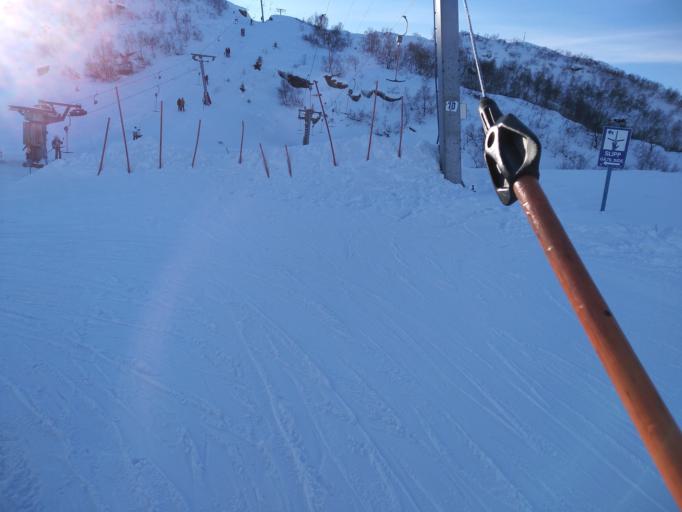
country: NO
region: Rogaland
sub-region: Sauda
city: Sauda
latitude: 59.6189
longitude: 6.2341
